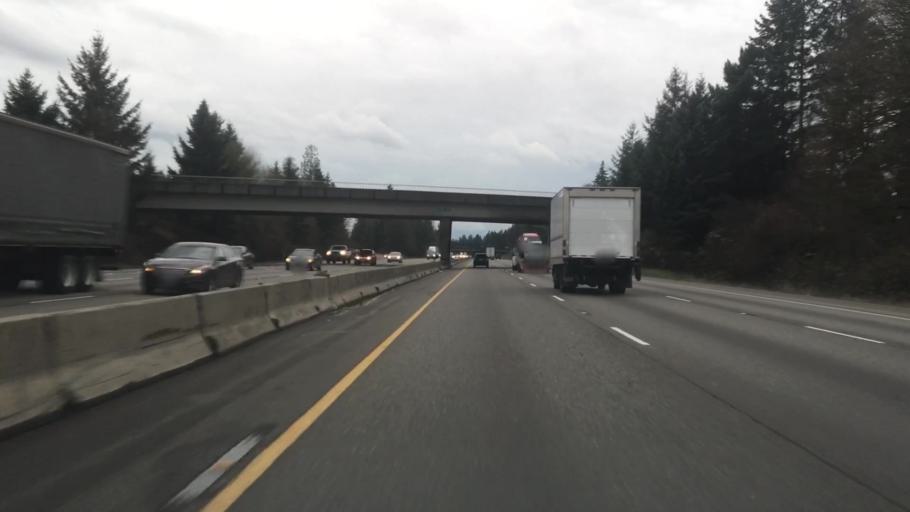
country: US
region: Washington
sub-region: Thurston County
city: Tumwater
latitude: 46.9862
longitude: -122.9225
